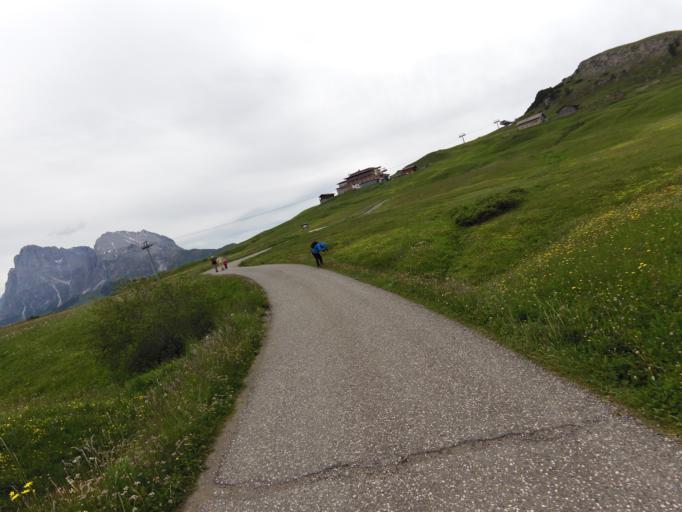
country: IT
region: Trentino-Alto Adige
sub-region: Bolzano
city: Ortisei
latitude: 46.5233
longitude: 11.6362
